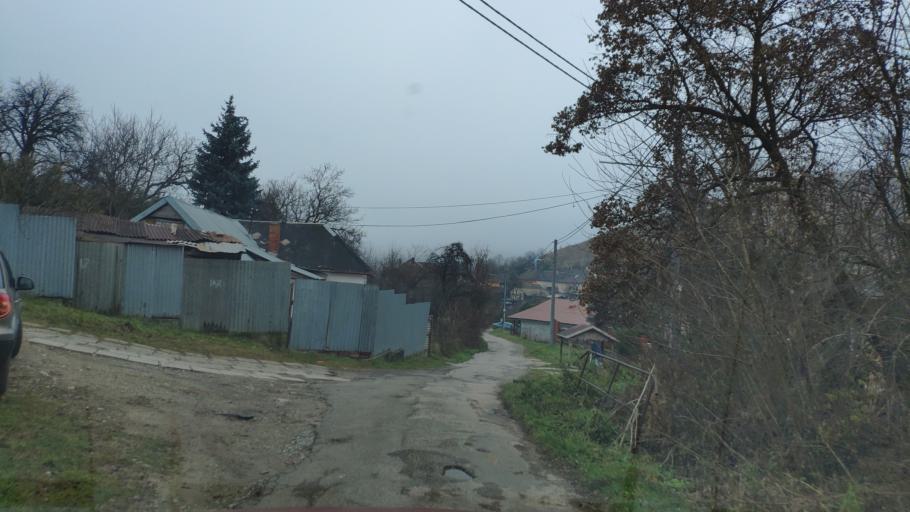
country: SK
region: Banskobystricky
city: Revuca
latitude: 48.6381
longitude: 20.2386
